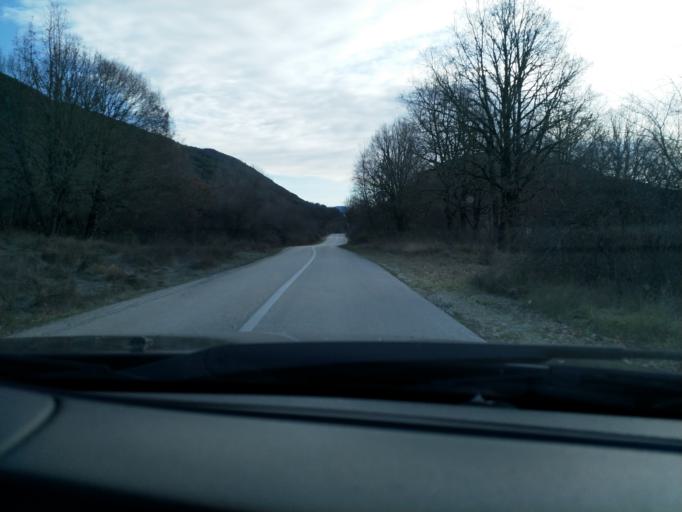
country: GR
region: Epirus
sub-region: Nomos Ioanninon
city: Asprangeloi
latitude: 39.8673
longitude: 20.7148
